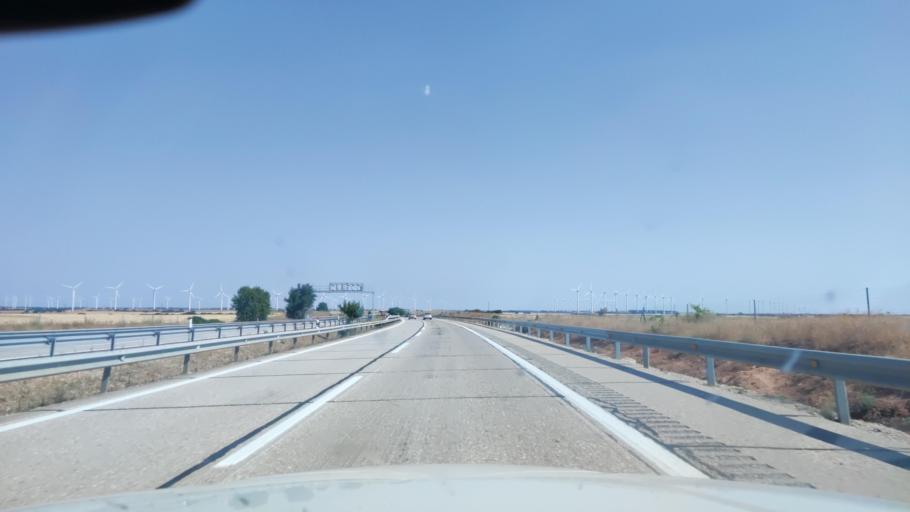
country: ES
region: Castille-La Mancha
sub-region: Provincia de Cuenca
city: Atalaya del Canavate
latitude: 39.4967
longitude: -2.2299
